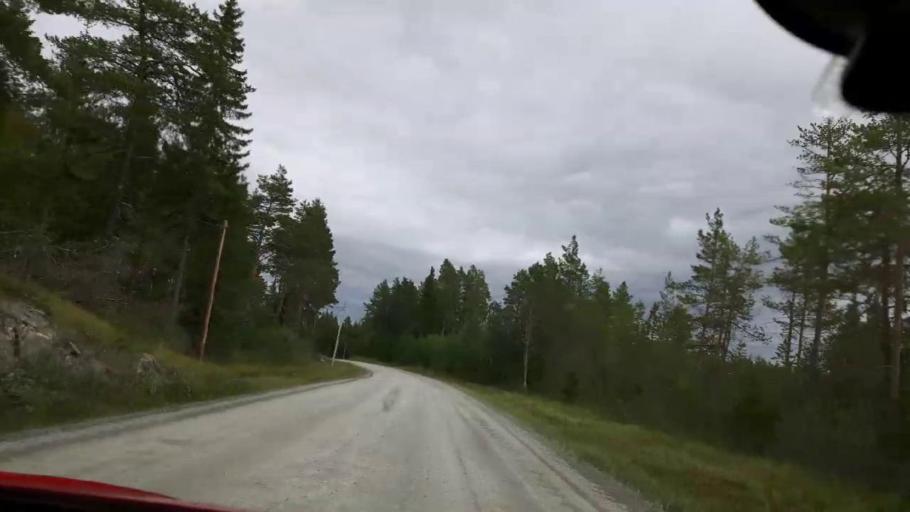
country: SE
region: Jaemtland
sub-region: OEstersunds Kommun
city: Brunflo
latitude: 63.1061
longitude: 15.0410
